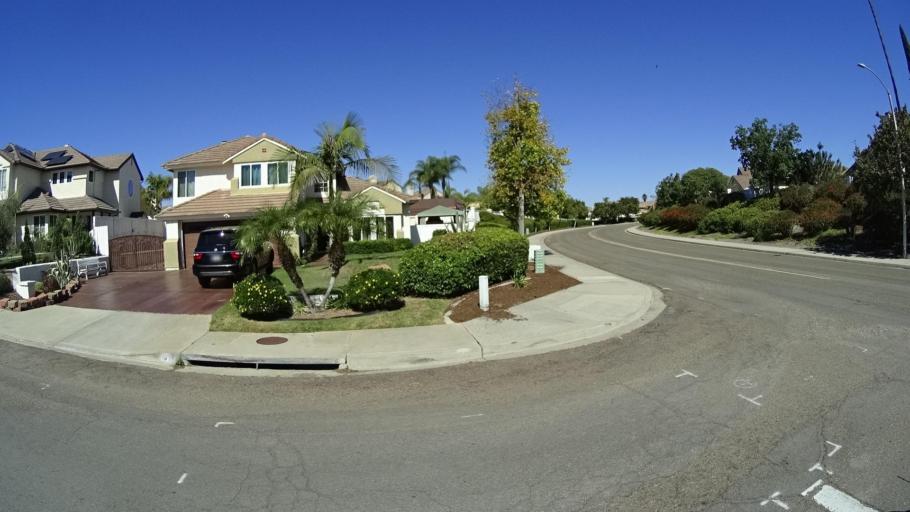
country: US
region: California
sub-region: San Diego County
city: Bonita
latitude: 32.6552
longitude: -116.9868
